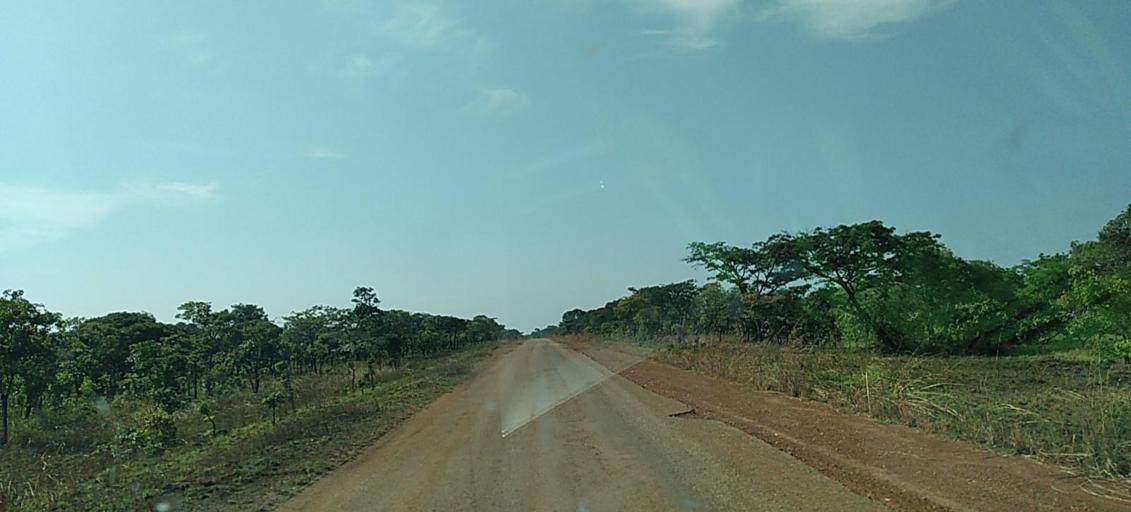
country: ZM
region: North-Western
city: Mwinilunga
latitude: -11.7942
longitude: 25.0719
